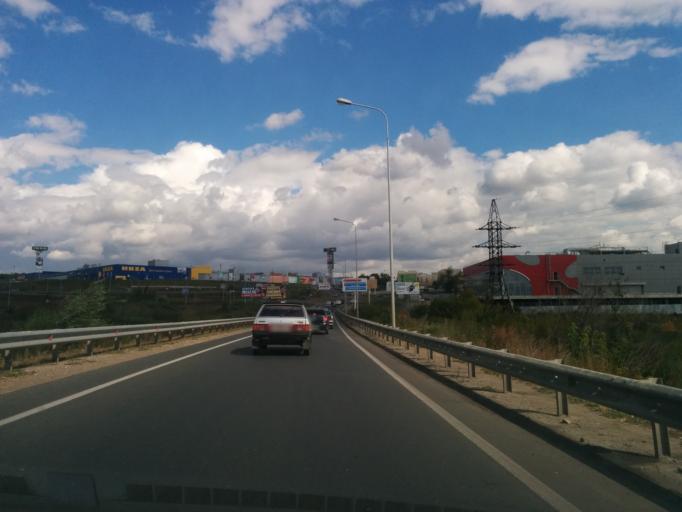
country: RU
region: Samara
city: Petra-Dubrava
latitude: 53.3196
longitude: 50.2974
